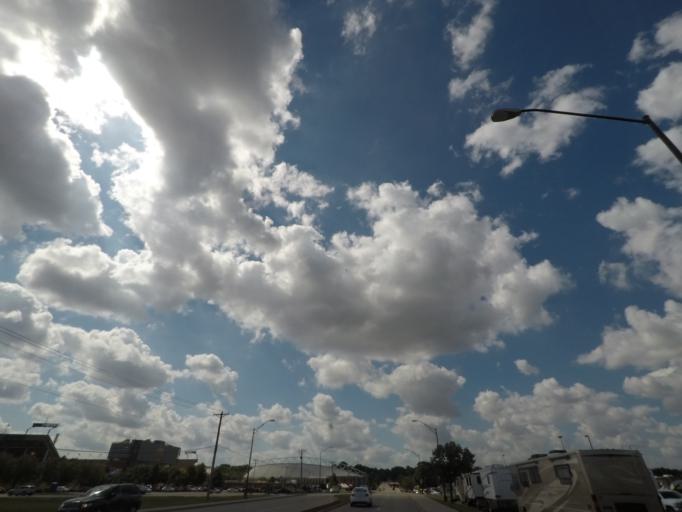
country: US
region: Iowa
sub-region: Story County
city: Ames
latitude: 42.0164
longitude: -93.6327
